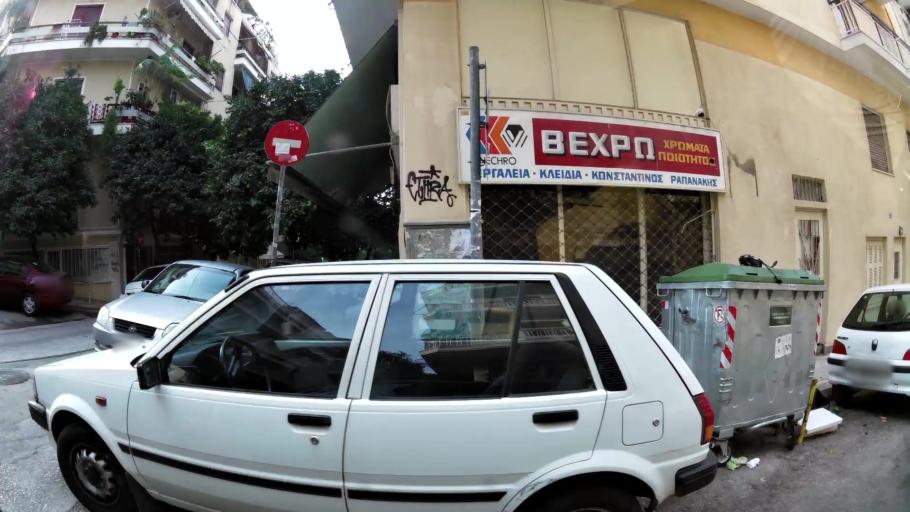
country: GR
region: Attica
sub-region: Nomarchia Athinas
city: Kipseli
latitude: 37.9938
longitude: 23.7468
